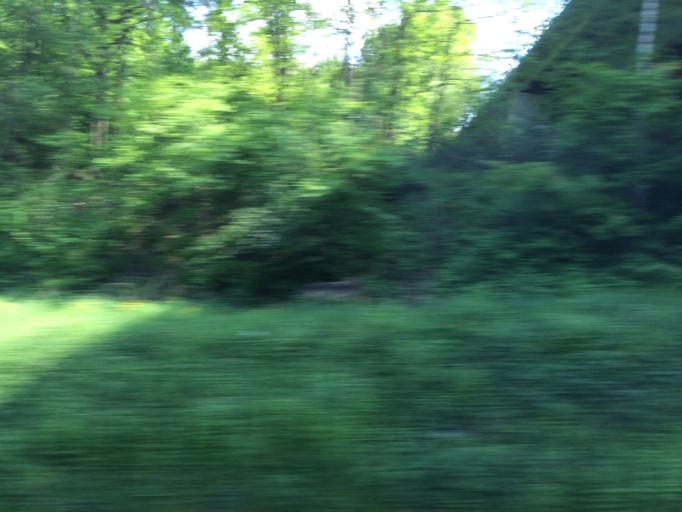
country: DE
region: Bavaria
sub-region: Regierungsbezirk Unterfranken
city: Rottendorf
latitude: 49.8022
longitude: 10.0488
